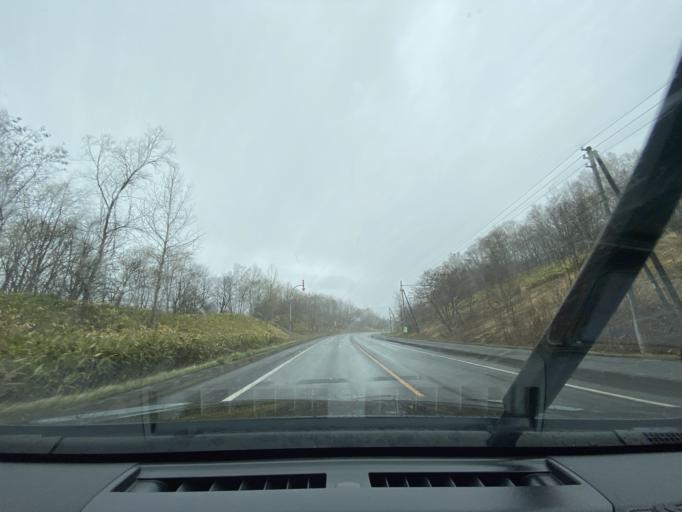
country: JP
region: Hokkaido
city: Fukagawa
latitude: 43.7149
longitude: 142.1743
